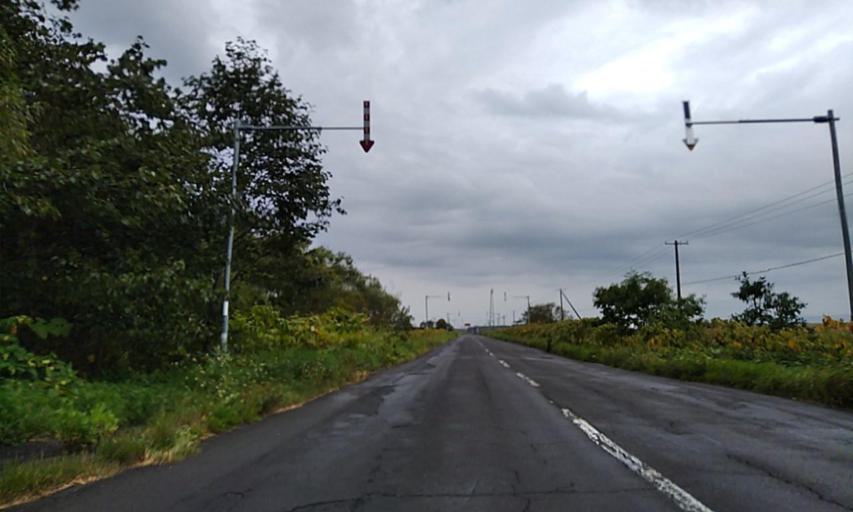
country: JP
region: Hokkaido
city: Nayoro
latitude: 44.6696
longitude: 142.8616
